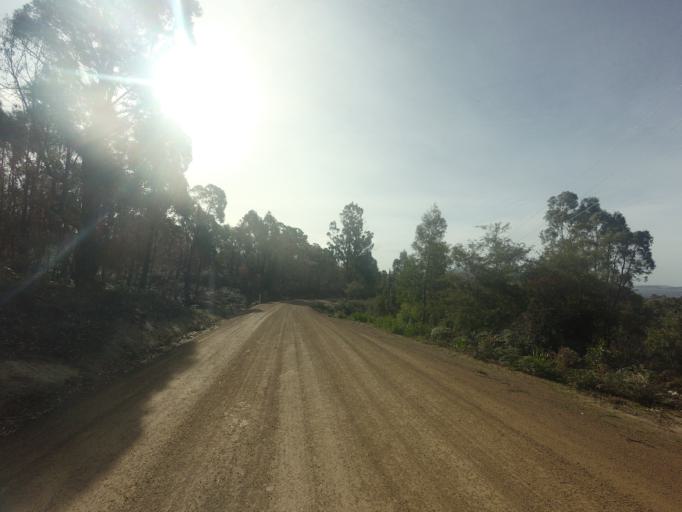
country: AU
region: Tasmania
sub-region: Kingborough
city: Kettering
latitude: -43.0810
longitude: 147.2634
